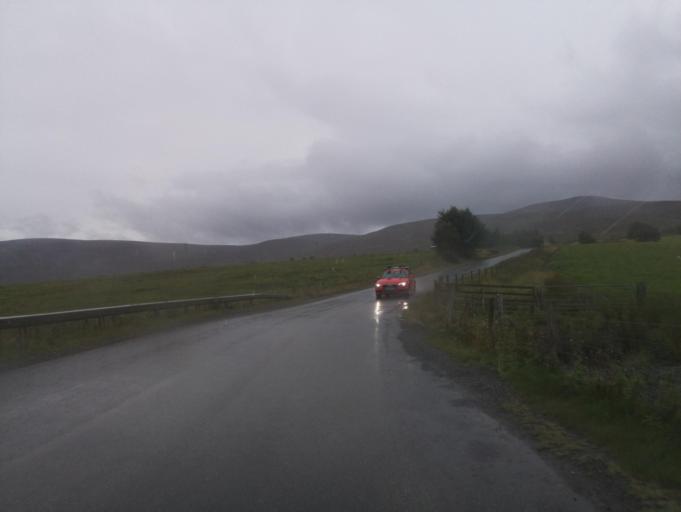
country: GB
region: Scotland
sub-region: Highland
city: Grantown on Spey
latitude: 57.3004
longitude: -3.5549
